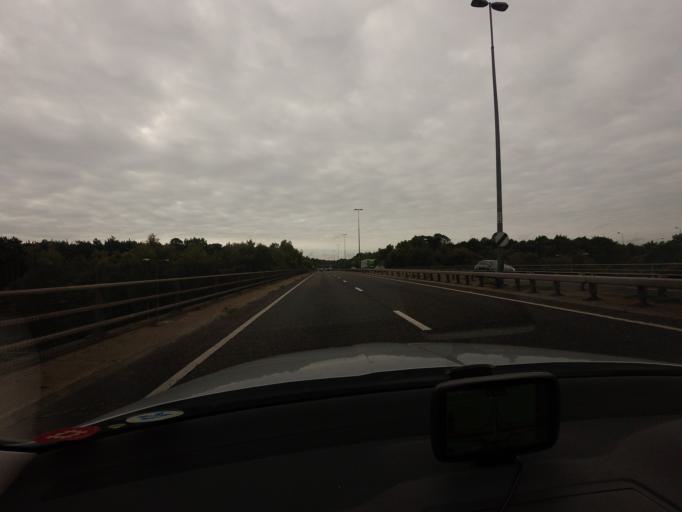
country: GB
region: England
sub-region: Surrey
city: Byfleet
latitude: 51.3224
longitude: -0.4501
